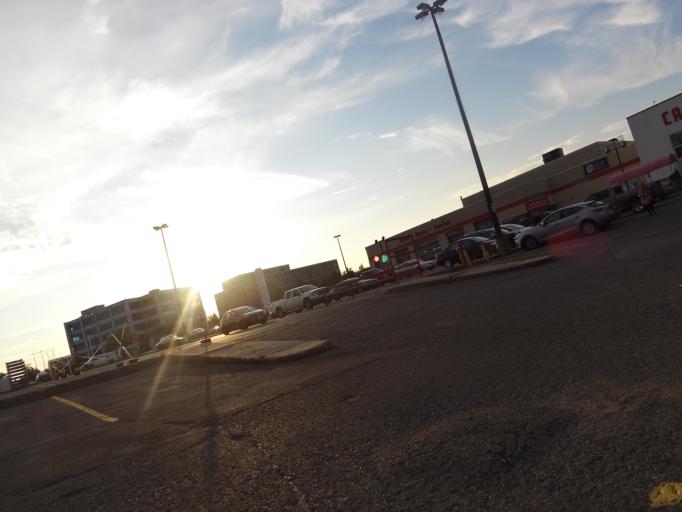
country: CA
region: Ontario
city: Bells Corners
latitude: 45.3218
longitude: -75.8353
